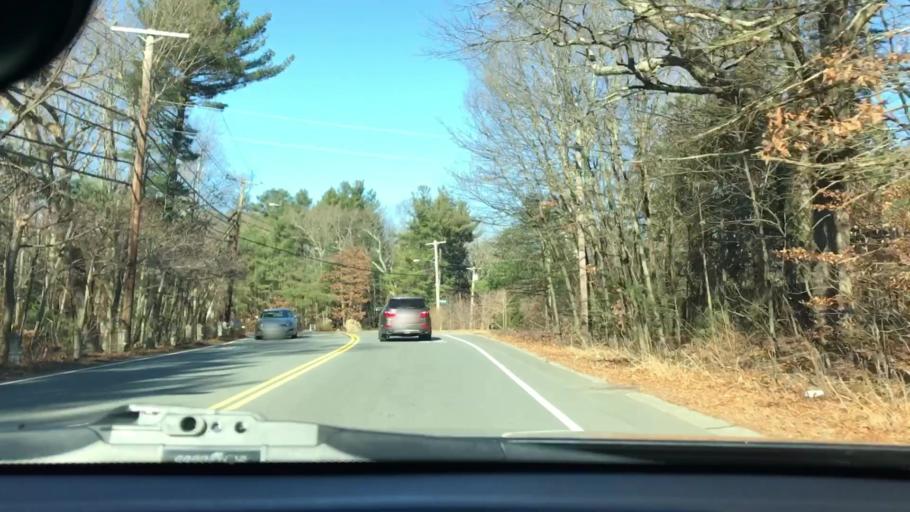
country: US
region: Massachusetts
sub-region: Norfolk County
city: Dedham
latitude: 42.2610
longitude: -71.1988
